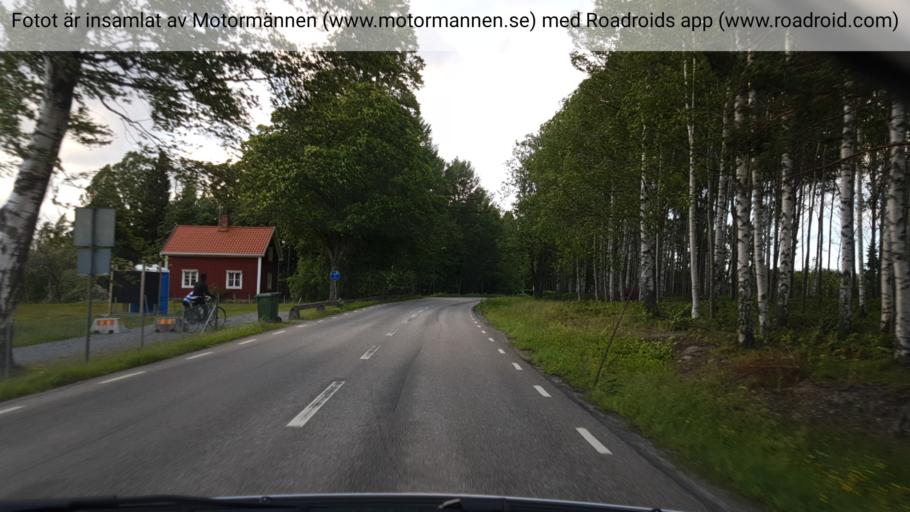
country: SE
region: OErebro
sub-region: Nora Kommun
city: As
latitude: 59.5000
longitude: 14.9574
